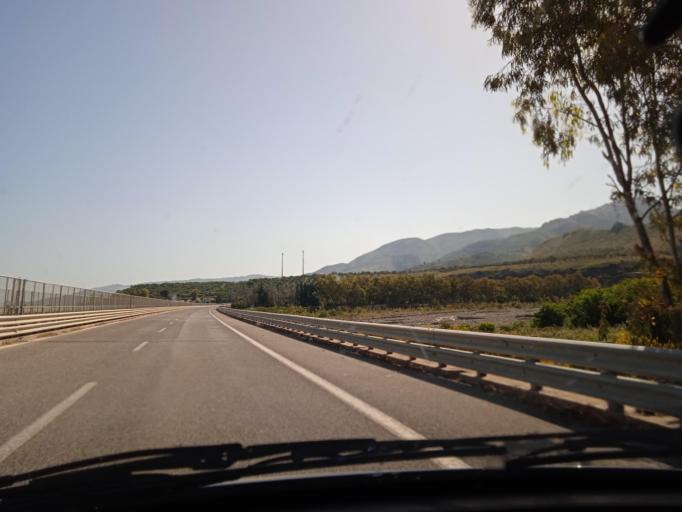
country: IT
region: Sicily
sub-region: Messina
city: Torrenova
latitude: 38.0766
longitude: 14.6621
